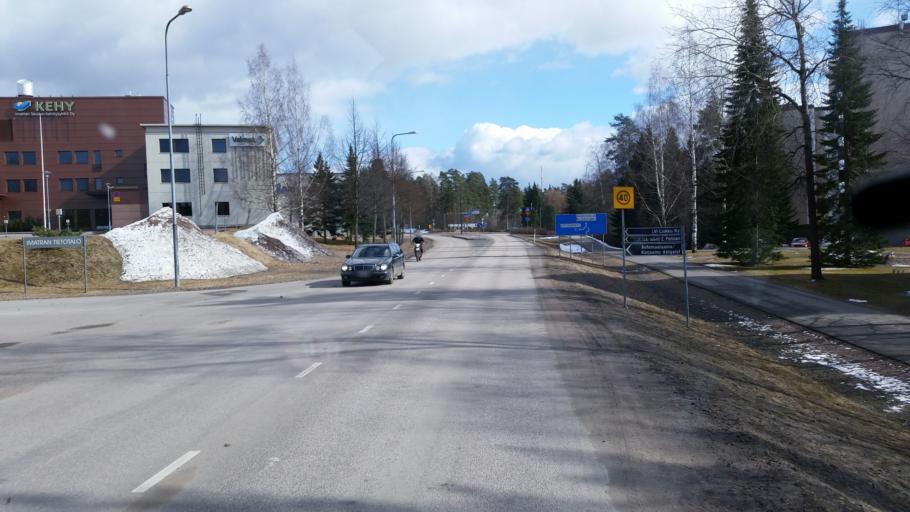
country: FI
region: South Karelia
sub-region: Imatra
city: Imatra
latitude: 61.1700
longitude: 28.7620
